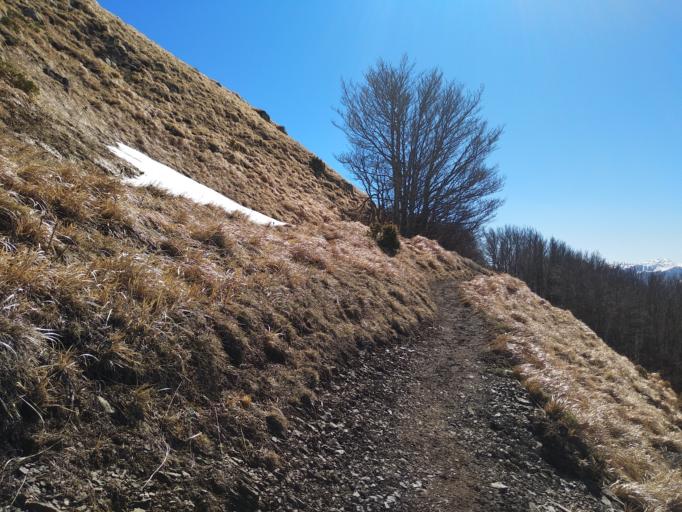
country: IT
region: Emilia-Romagna
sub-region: Provincia di Reggio Emilia
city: Collagna
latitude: 44.3735
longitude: 10.2849
